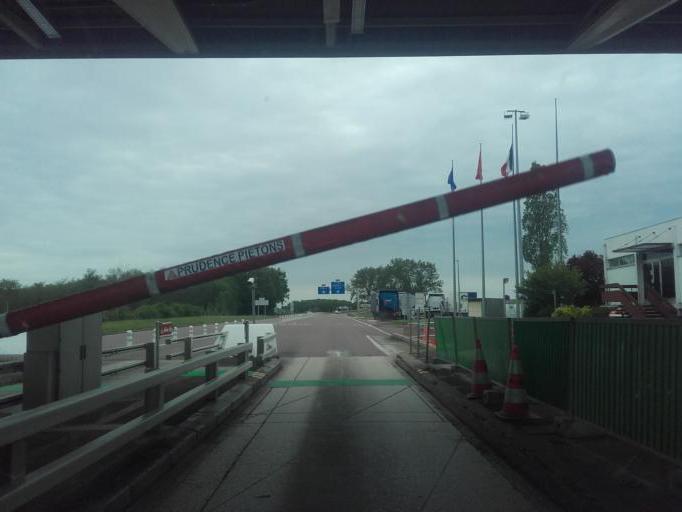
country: FR
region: Bourgogne
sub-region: Departement de l'Yonne
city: Venoy
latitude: 47.7968
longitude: 3.6531
